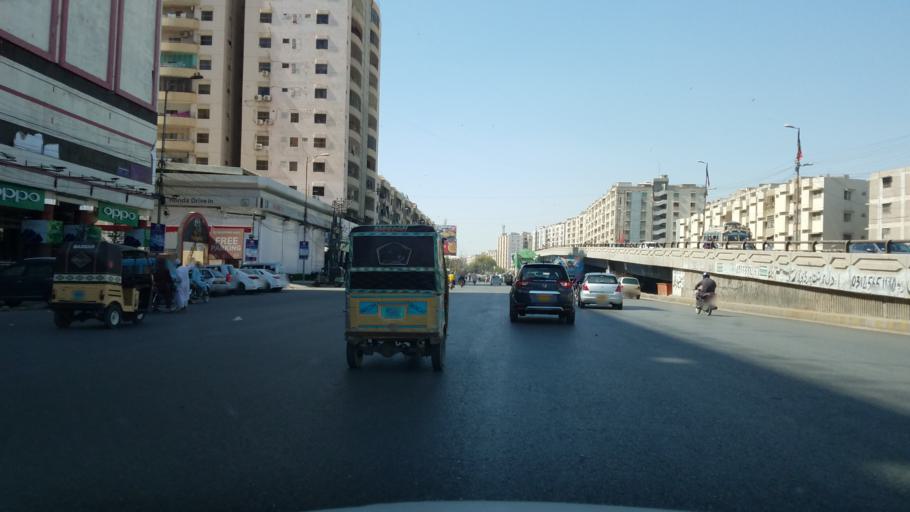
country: PK
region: Sindh
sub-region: Karachi District
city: Karachi
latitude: 24.9030
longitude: 67.1146
